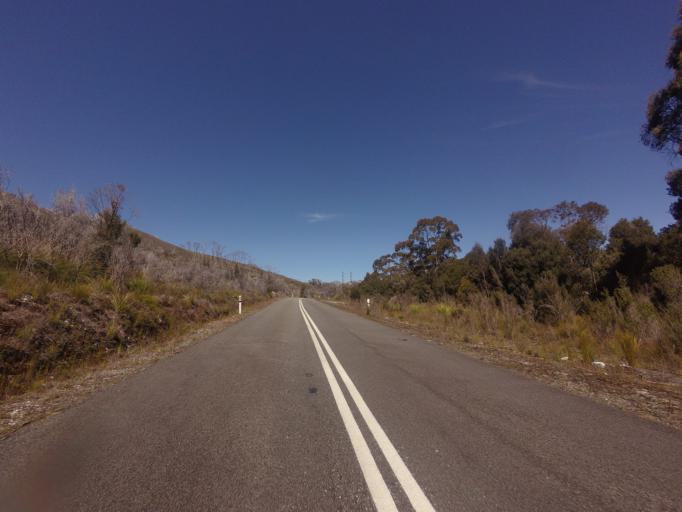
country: AU
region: Tasmania
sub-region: Huon Valley
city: Geeveston
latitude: -42.8358
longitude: 146.1560
